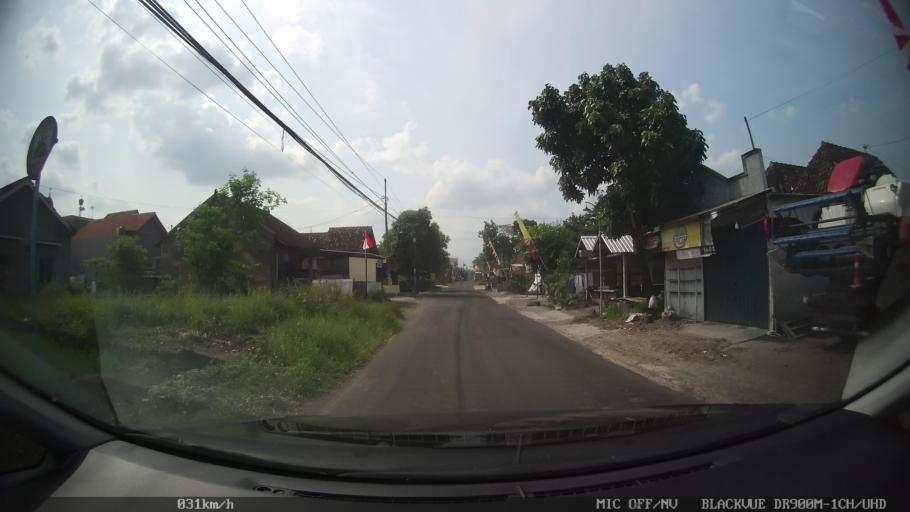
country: ID
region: Daerah Istimewa Yogyakarta
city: Depok
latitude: -7.7963
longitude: 110.4455
